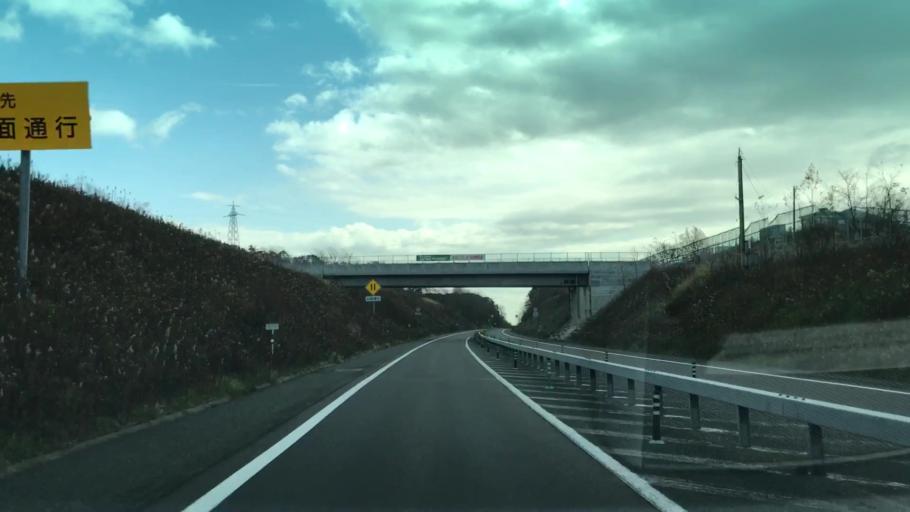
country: JP
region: Hokkaido
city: Shizunai-furukawacho
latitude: 42.5407
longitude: 142.0162
